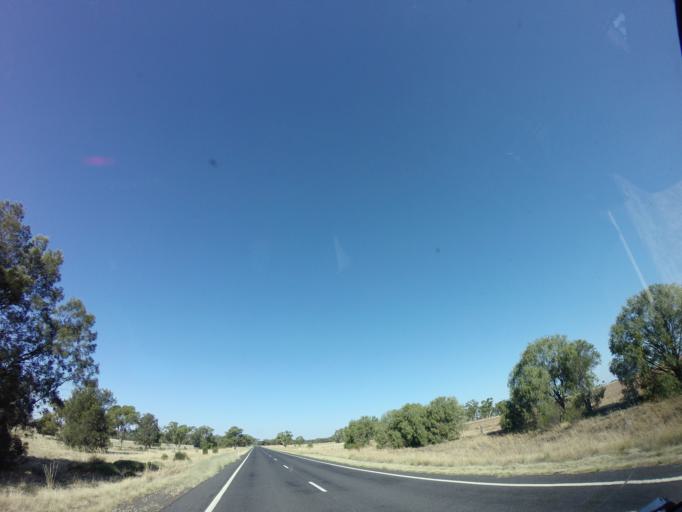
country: AU
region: New South Wales
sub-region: Gilgandra
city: Gilgandra
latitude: -31.6614
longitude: 148.3322
